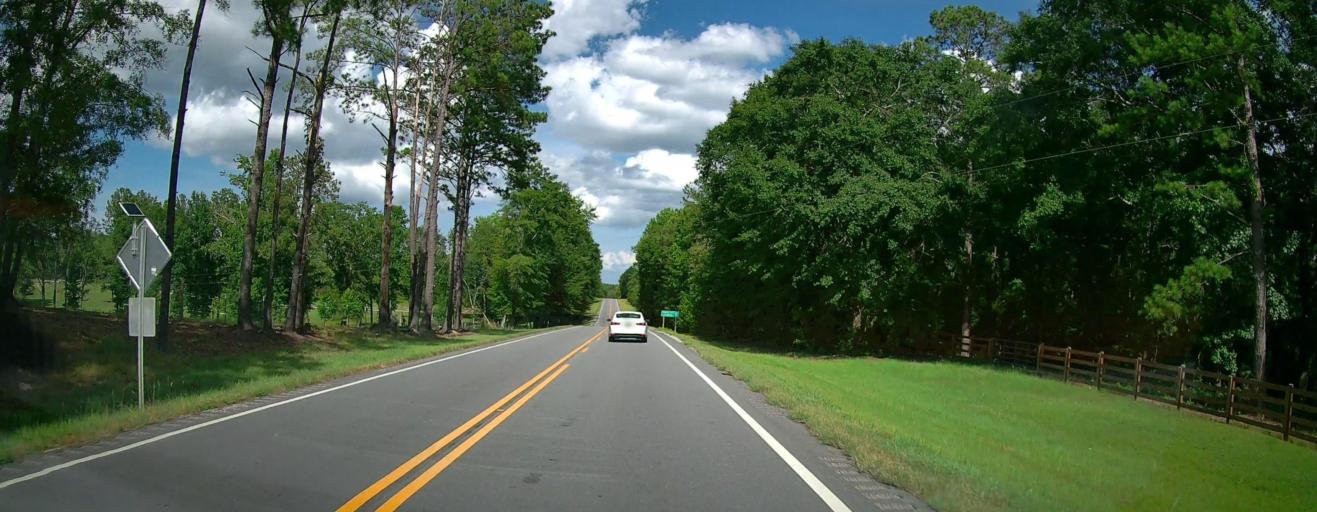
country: US
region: Alabama
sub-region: Lee County
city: Opelika
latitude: 32.4391
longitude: -85.3610
